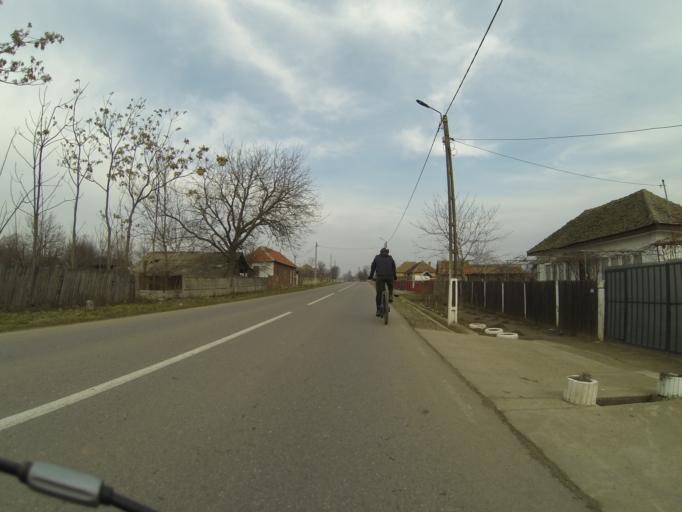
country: RO
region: Mehedinti
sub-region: Comuna Corlatel
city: Corlatel
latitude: 44.3980
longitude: 22.9286
